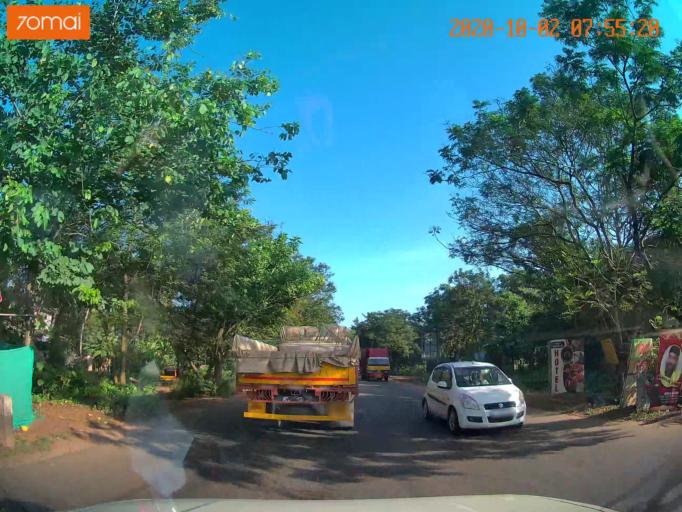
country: IN
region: Kerala
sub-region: Kozhikode
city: Ferokh
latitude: 11.1819
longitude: 75.8719
